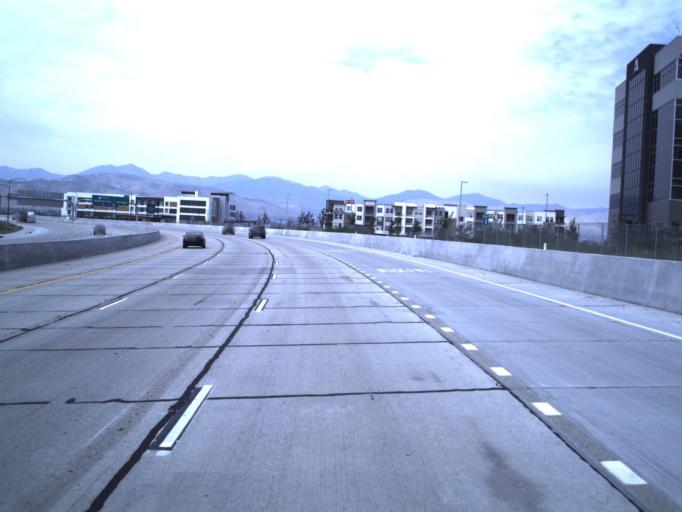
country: US
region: Utah
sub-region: Salt Lake County
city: Bluffdale
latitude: 40.5044
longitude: -111.9002
